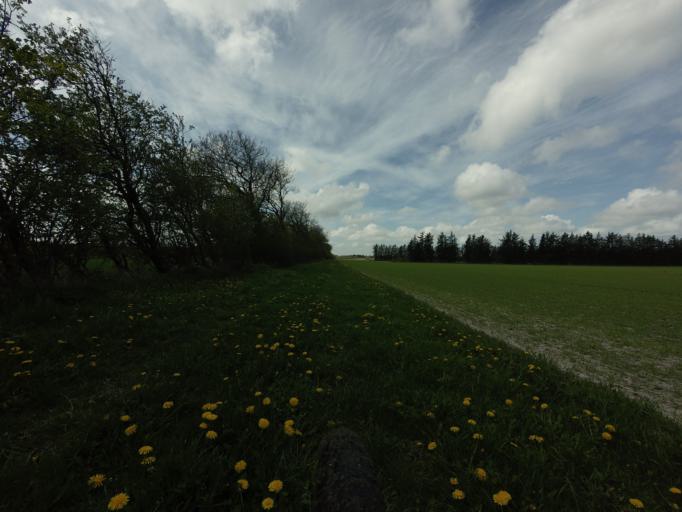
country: DK
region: North Denmark
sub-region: Jammerbugt Kommune
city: Kas
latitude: 57.1966
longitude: 9.6177
